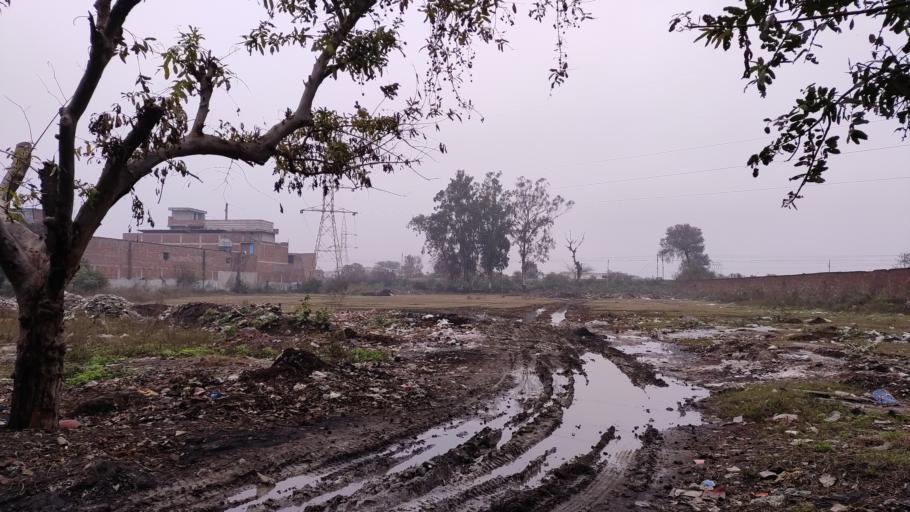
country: IN
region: Punjab
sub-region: Amritsar
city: Amritsar
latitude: 31.6219
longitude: 74.9251
